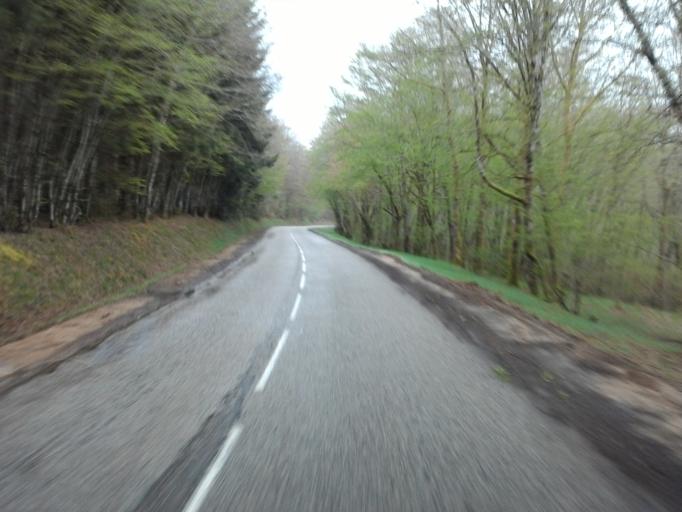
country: FR
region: Bourgogne
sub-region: Departement de la Cote-d'Or
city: Saulieu
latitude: 47.2468
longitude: 4.0511
